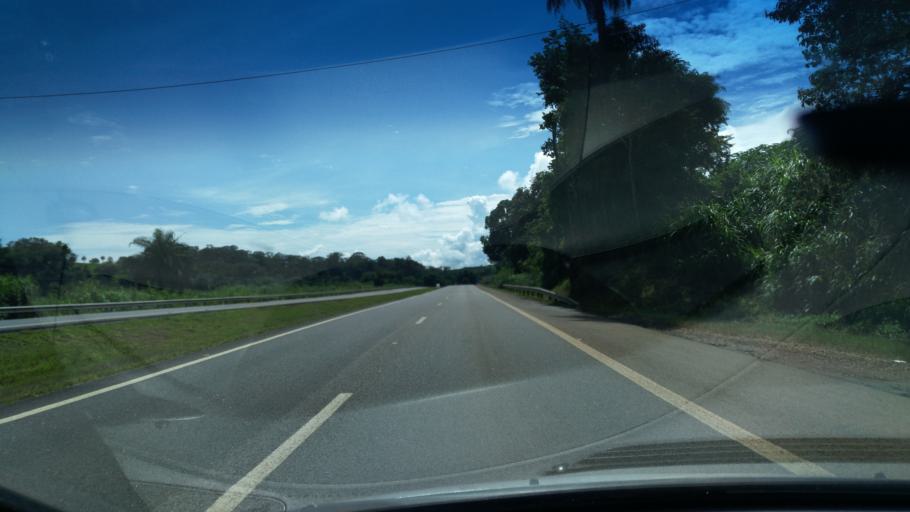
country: BR
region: Sao Paulo
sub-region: Santo Antonio Do Jardim
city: Espirito Santo do Pinhal
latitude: -22.2288
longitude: -46.7949
